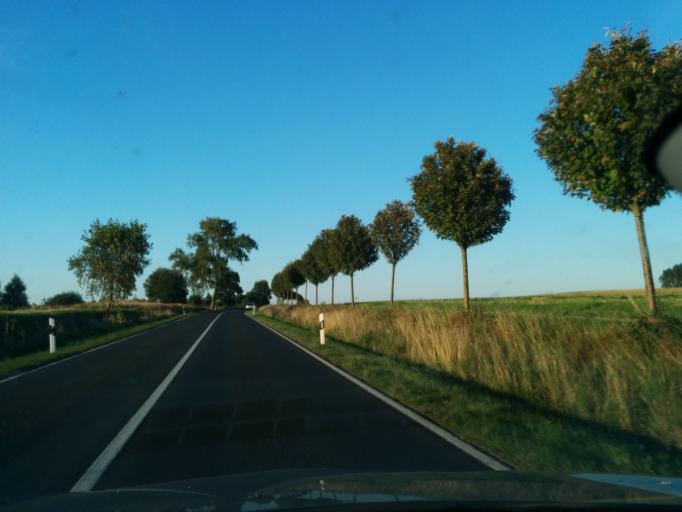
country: DE
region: Mecklenburg-Vorpommern
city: Loddin
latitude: 53.9470
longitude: 14.0479
